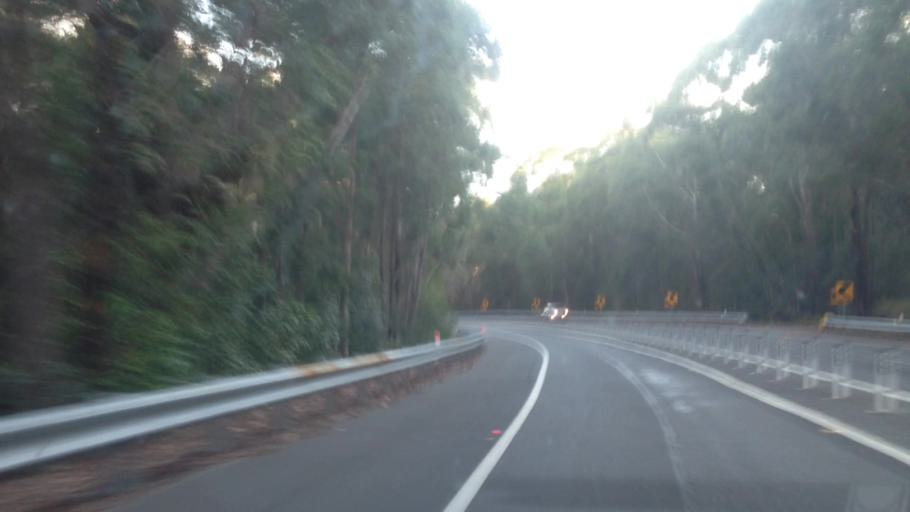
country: AU
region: New South Wales
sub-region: Lake Macquarie Shire
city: Cooranbong
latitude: -32.9733
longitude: 151.4820
